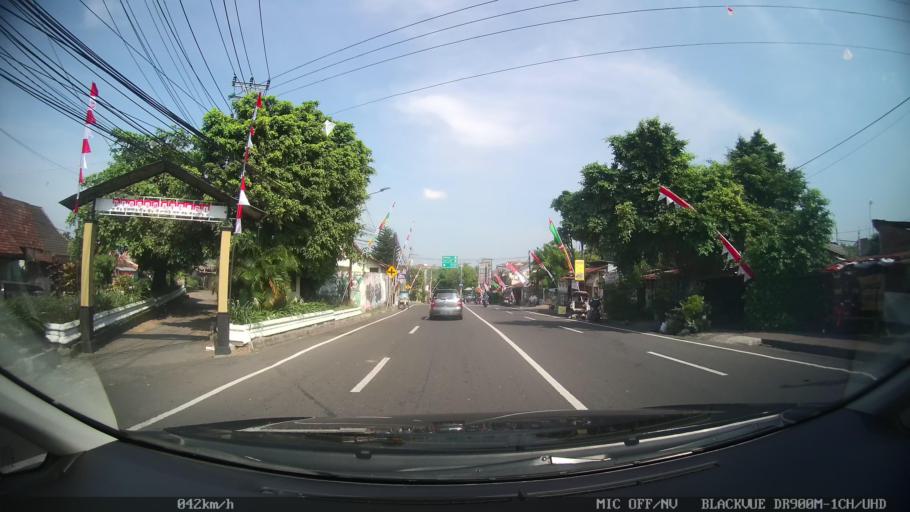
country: ID
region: Daerah Istimewa Yogyakarta
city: Yogyakarta
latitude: -7.7895
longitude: 110.3588
